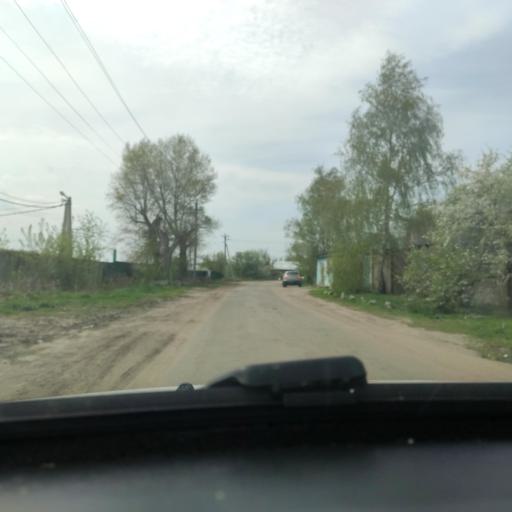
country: RU
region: Voronezj
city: Pridonskoy
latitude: 51.7338
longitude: 39.0606
